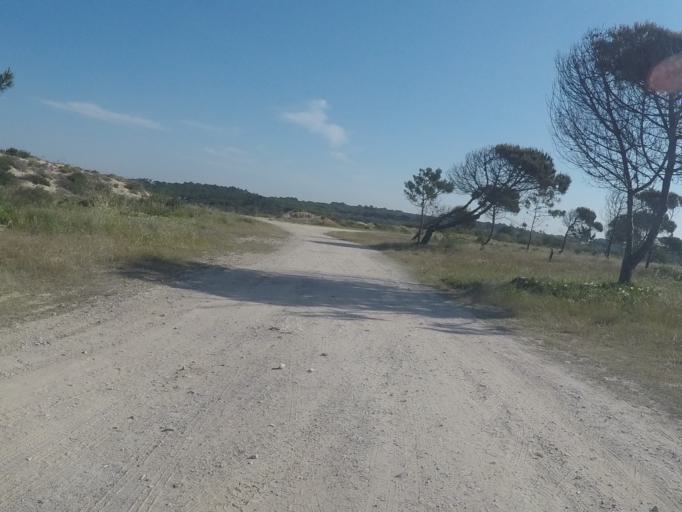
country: PT
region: Setubal
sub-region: Sesimbra
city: Sesimbra
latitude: 38.4920
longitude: -9.1806
